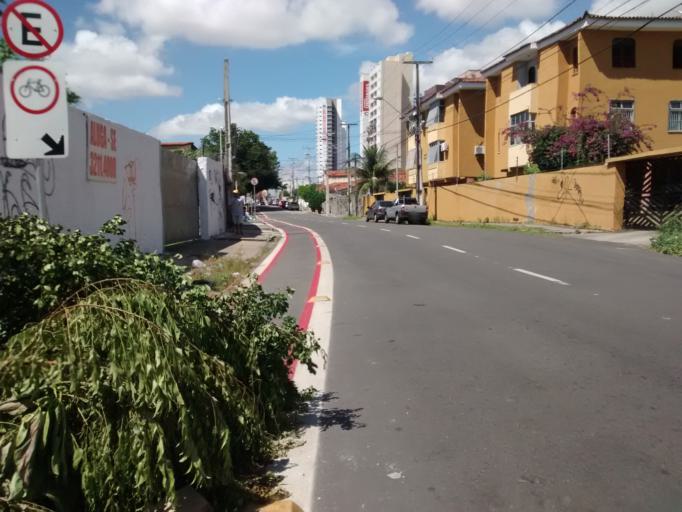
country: BR
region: Ceara
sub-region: Fortaleza
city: Fortaleza
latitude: -3.7316
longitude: -38.5597
